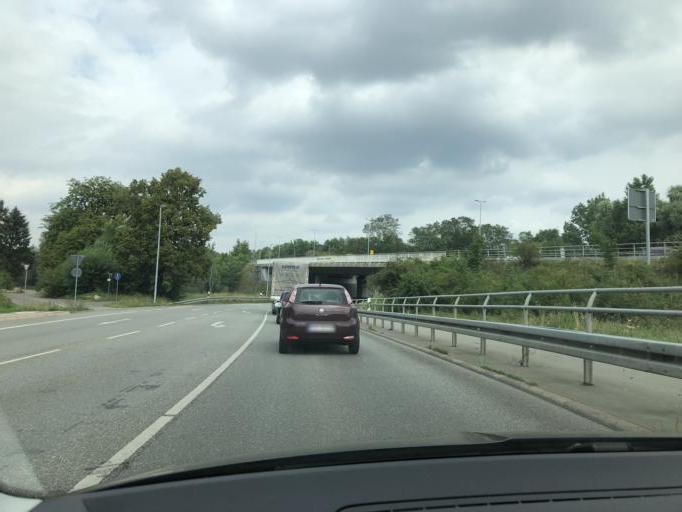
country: DE
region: Mecklenburg-Vorpommern
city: Neumuehle
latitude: 53.6249
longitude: 11.3614
